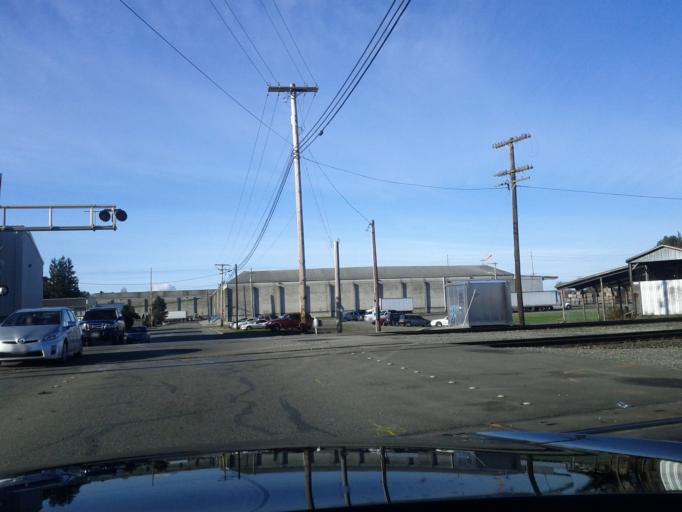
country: US
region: Washington
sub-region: Skagit County
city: Burlington
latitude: 48.4733
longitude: -122.3288
